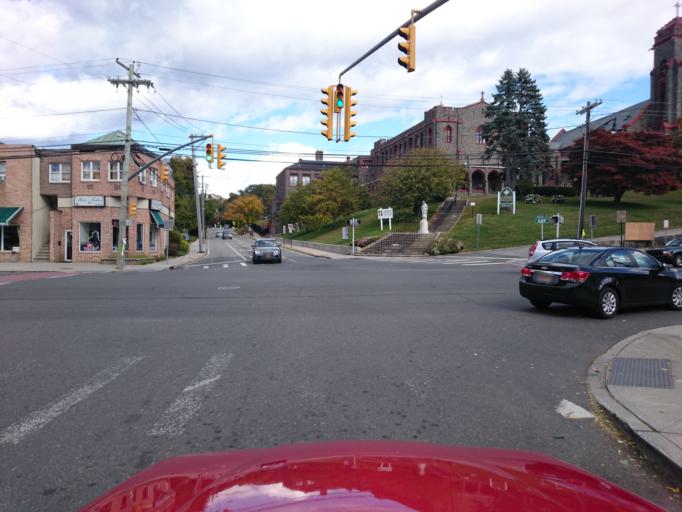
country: US
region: New York
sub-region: Nassau County
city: Glen Cove
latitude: 40.8610
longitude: -73.6228
